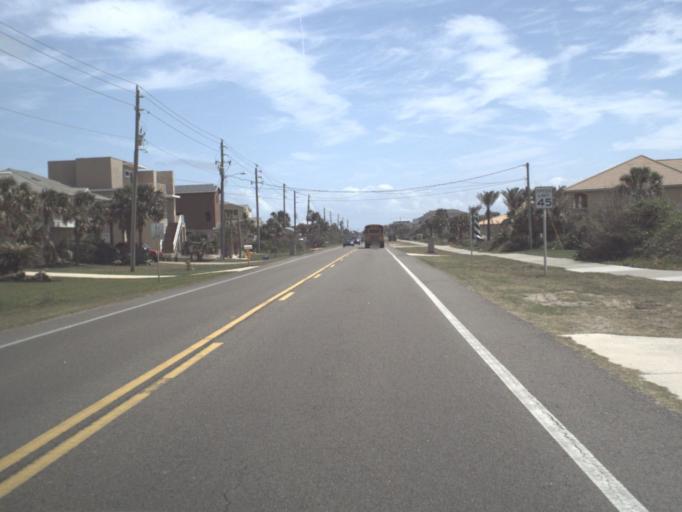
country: US
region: Florida
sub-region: Flagler County
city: Flagler Beach
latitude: 29.5201
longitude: -81.1471
